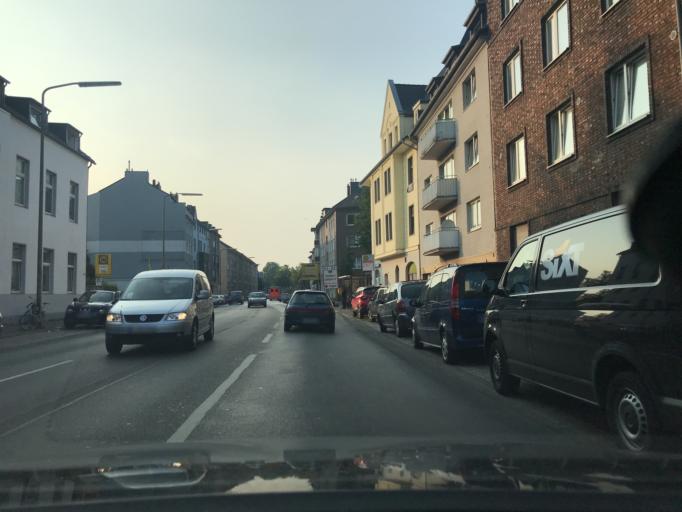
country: DE
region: North Rhine-Westphalia
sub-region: Regierungsbezirk Dusseldorf
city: Ratingen
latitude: 51.2579
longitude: 6.8182
